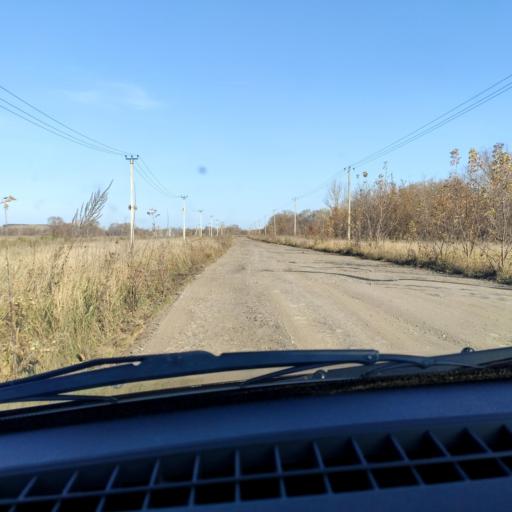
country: RU
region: Bashkortostan
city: Avdon
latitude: 54.4981
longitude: 55.8692
